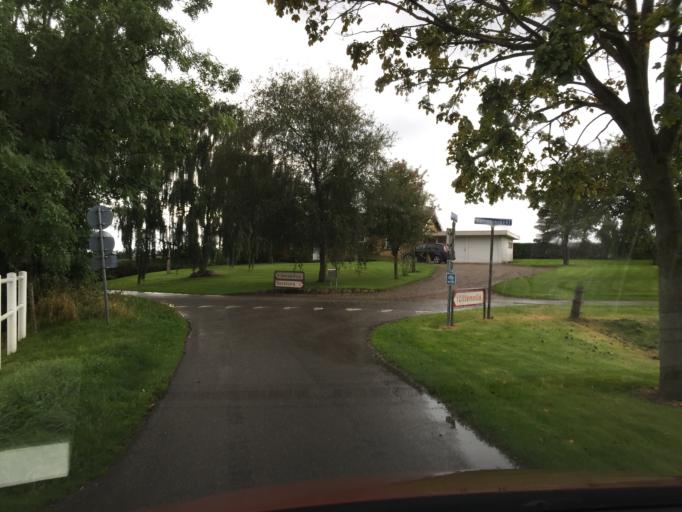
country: DK
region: South Denmark
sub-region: Sonderborg Kommune
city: Dybbol
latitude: 54.9329
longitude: 9.7443
